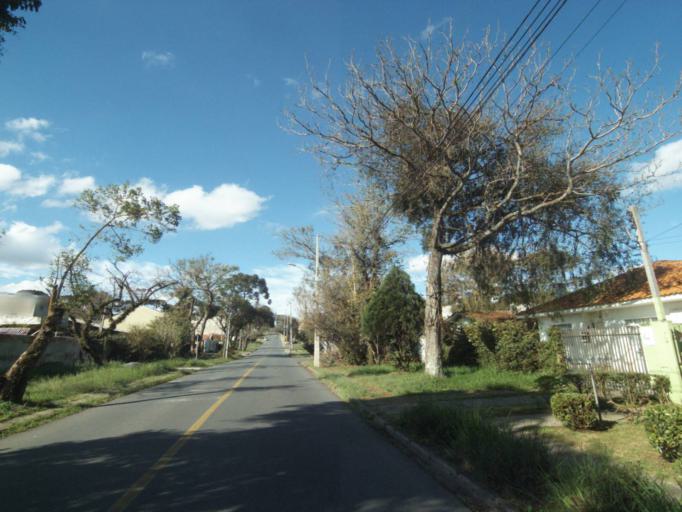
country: BR
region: Parana
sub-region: Curitiba
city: Curitiba
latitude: -25.3831
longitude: -49.2460
